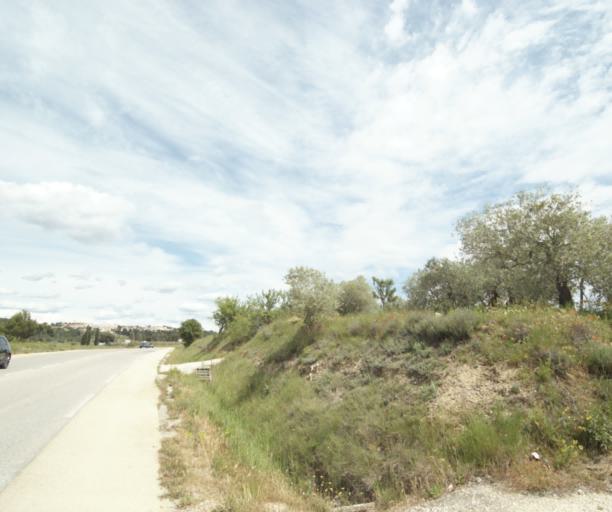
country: FR
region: Provence-Alpes-Cote d'Azur
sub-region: Departement des Bouches-du-Rhone
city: Velaux
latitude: 43.5112
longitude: 5.2419
